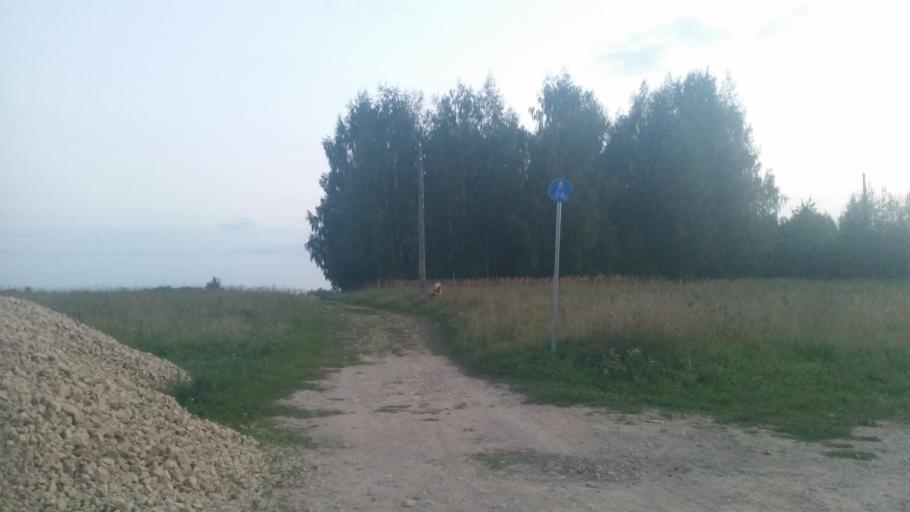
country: LV
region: Ogre
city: Ogre
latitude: 56.8138
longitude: 24.5874
